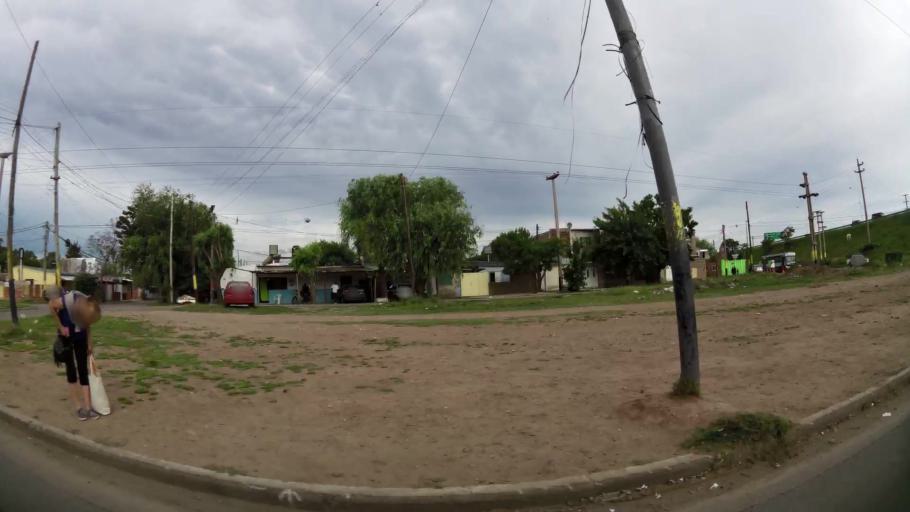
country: AR
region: Santa Fe
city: Gobernador Galvez
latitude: -33.0001
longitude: -60.6892
